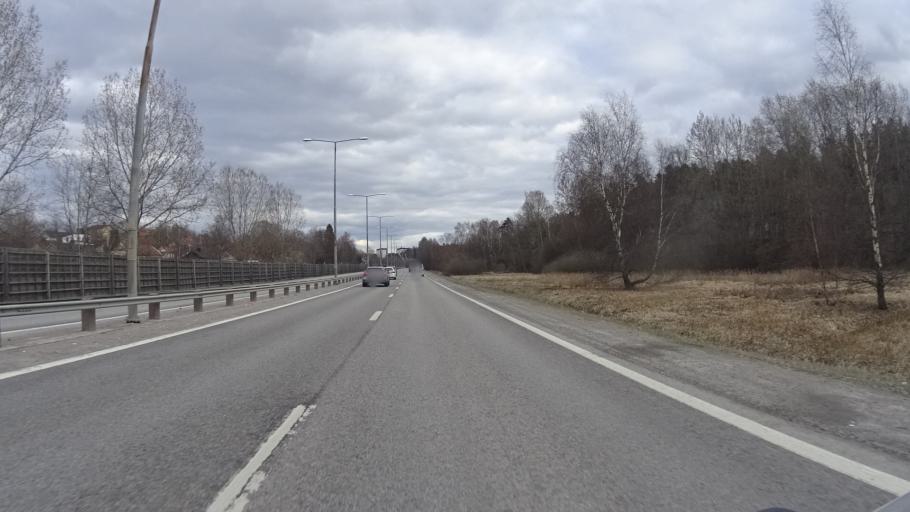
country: SE
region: Stockholm
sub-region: Stockholms Kommun
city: Arsta
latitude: 59.2702
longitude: 18.0173
